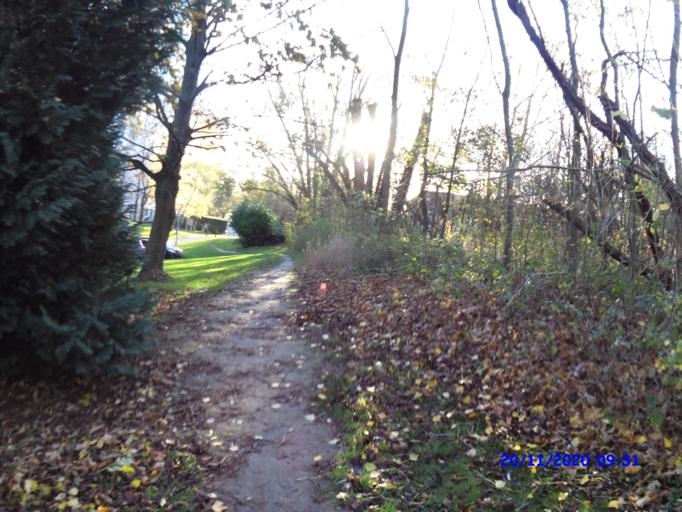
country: BE
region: Flanders
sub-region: Provincie Vlaams-Brabant
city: Kraainem
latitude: 50.8522
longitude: 4.4309
